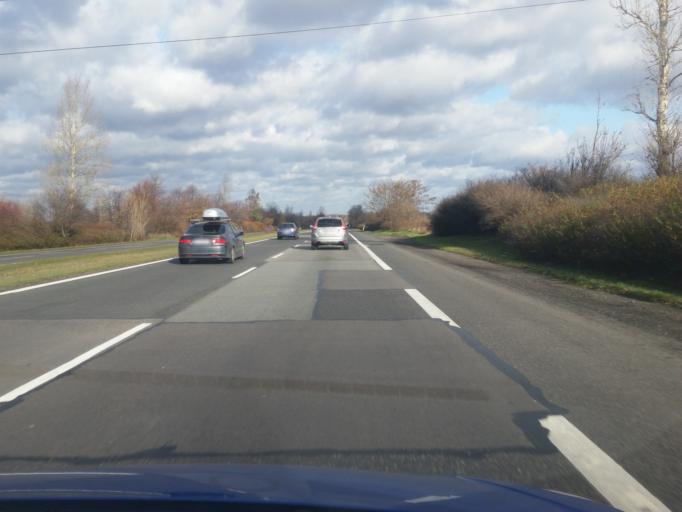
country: PL
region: Silesian Voivodeship
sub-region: Powiat czestochowski
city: Redziny
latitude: 50.8559
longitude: 19.1530
